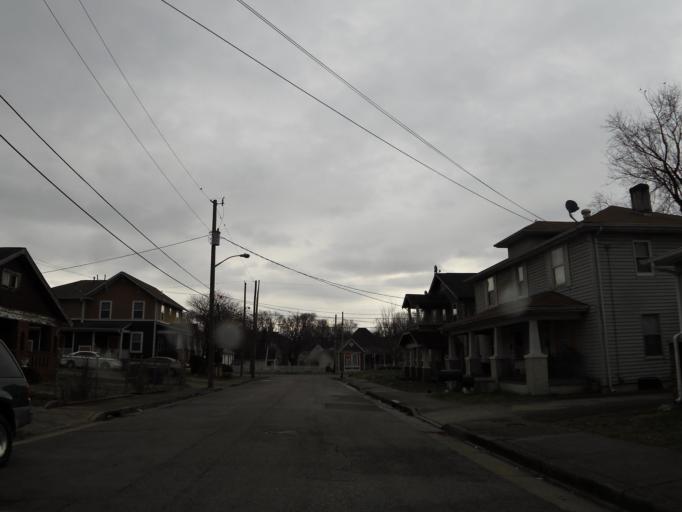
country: US
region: Tennessee
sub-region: Knox County
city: Knoxville
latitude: 35.9700
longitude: -83.9370
